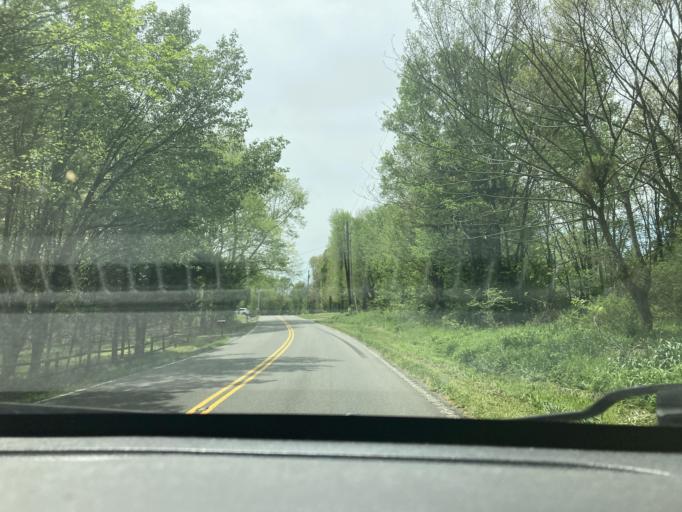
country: US
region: Tennessee
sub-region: Dickson County
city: Dickson
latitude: 36.1053
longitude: -87.3782
